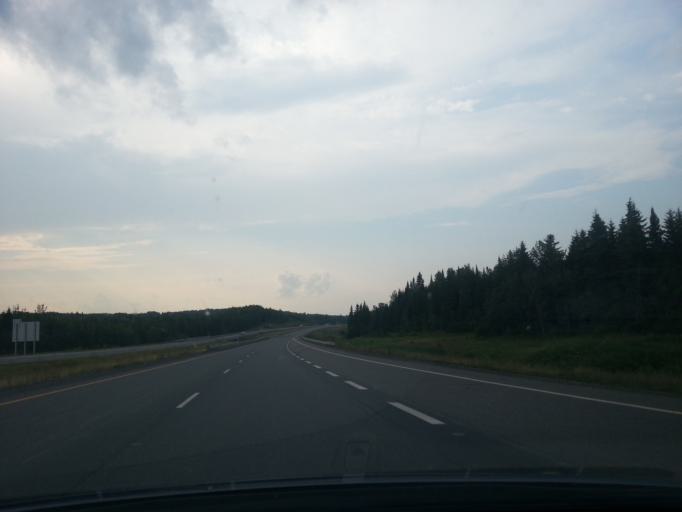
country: CA
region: New Brunswick
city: Harrison Brook
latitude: 47.2309
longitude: -67.9610
